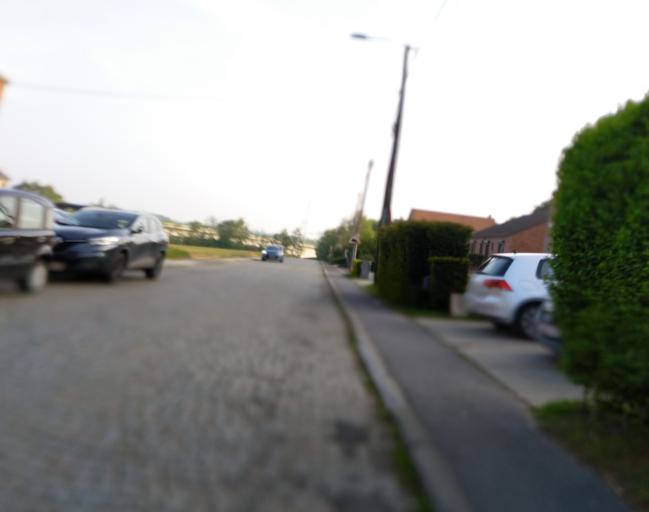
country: BE
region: Wallonia
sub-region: Province du Hainaut
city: Roeulx
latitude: 50.4739
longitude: 4.0366
